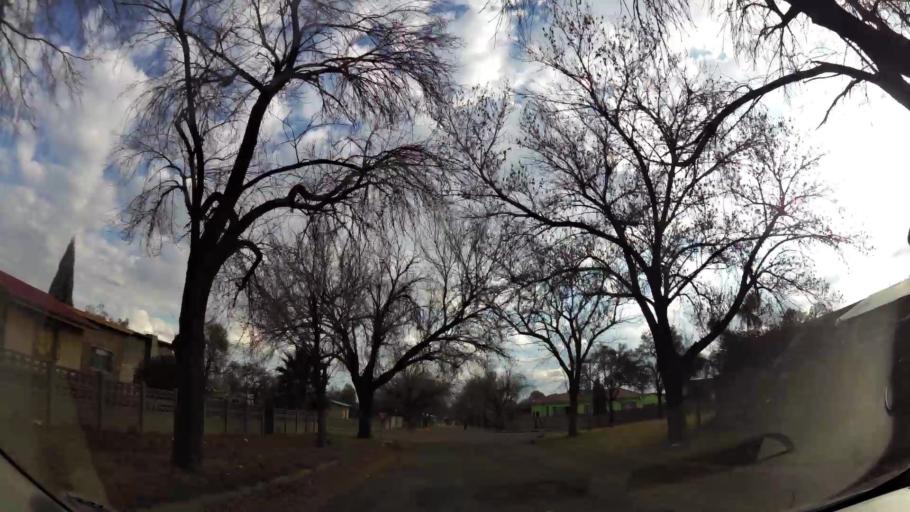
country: ZA
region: Orange Free State
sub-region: Fezile Dabi District Municipality
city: Sasolburg
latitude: -26.8248
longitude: 27.8274
